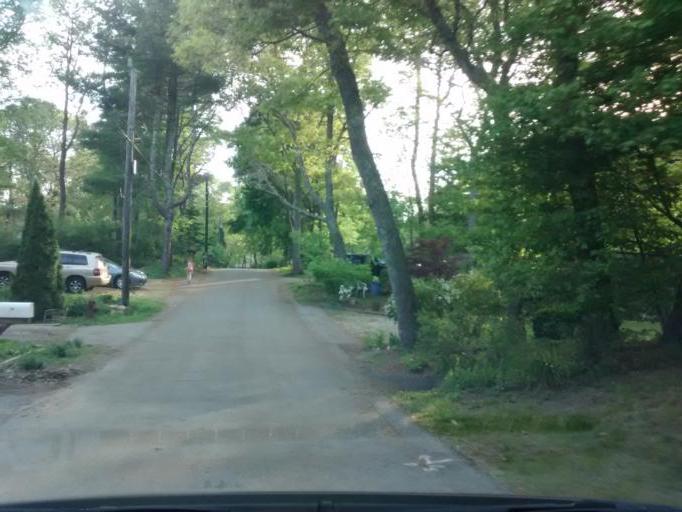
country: US
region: Massachusetts
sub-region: Barnstable County
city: East Falmouth
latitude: 41.6000
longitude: -70.5841
